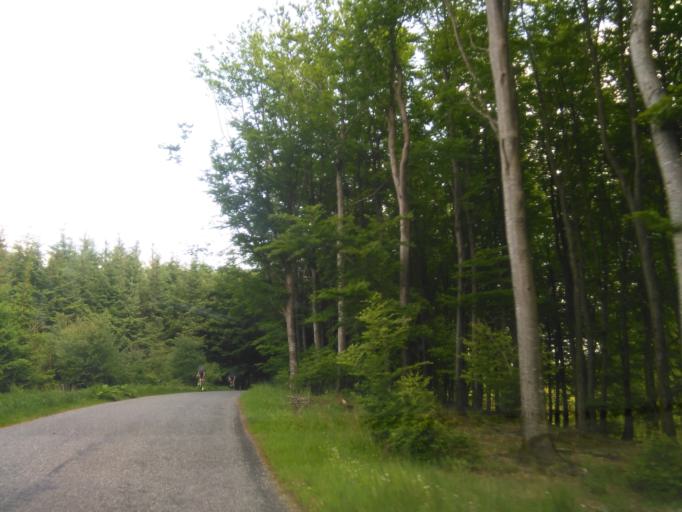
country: DK
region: Central Jutland
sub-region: Favrskov Kommune
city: Hammel
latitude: 56.2311
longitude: 9.9295
